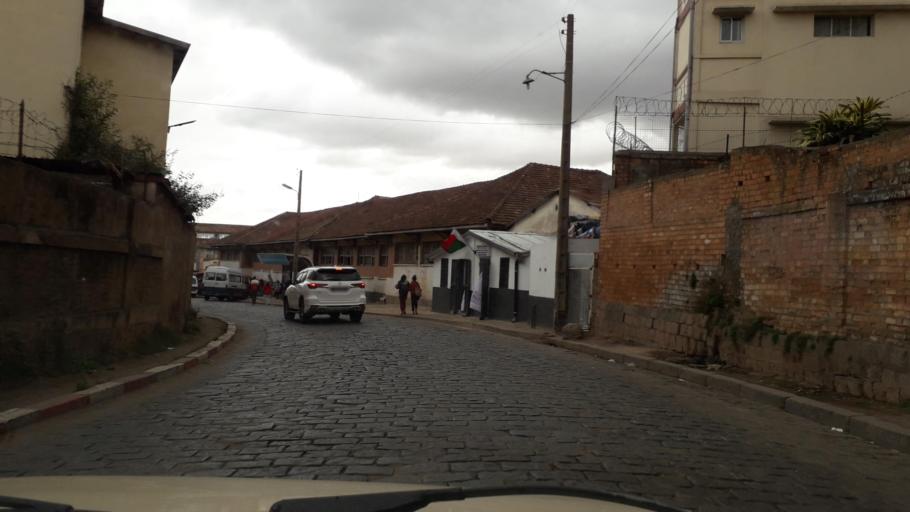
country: MG
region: Analamanga
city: Antananarivo
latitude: -18.8977
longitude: 47.5200
